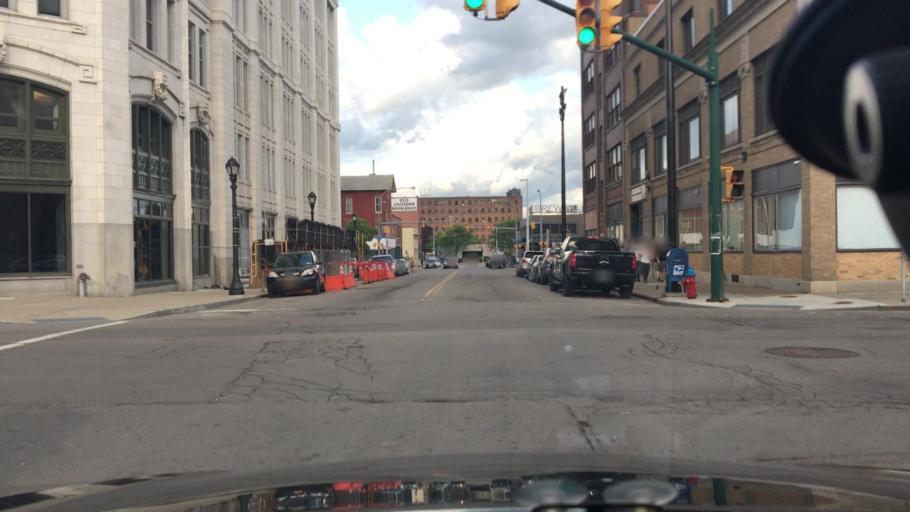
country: US
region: New York
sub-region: Erie County
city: Buffalo
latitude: 42.8885
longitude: -78.8726
